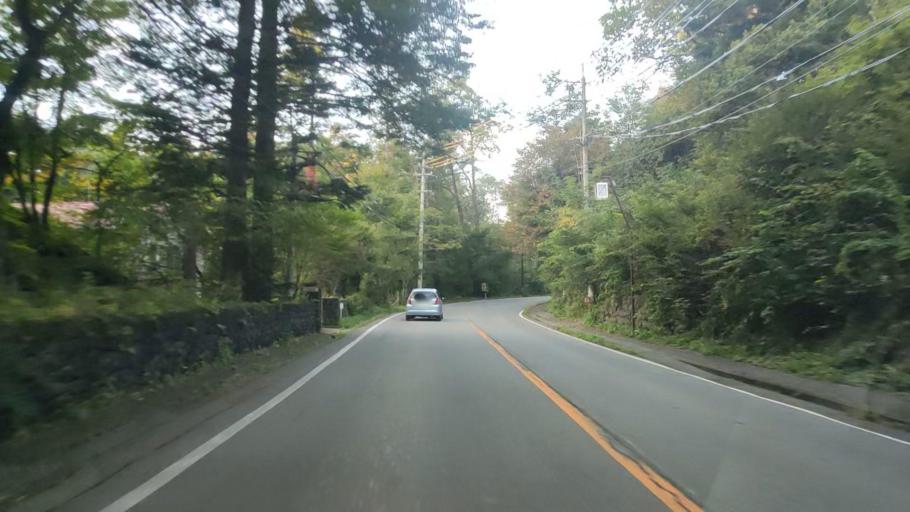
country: JP
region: Nagano
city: Komoro
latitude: 36.3629
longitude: 138.5877
